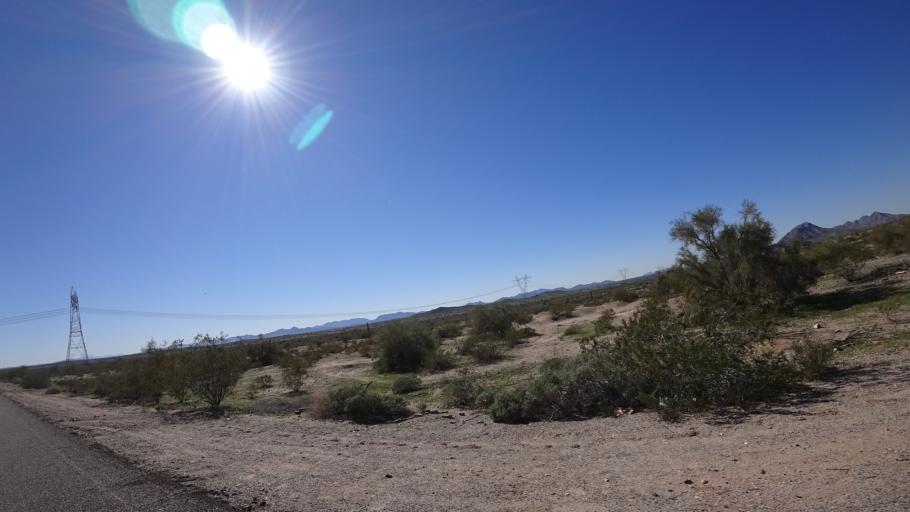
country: US
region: Arizona
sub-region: Maricopa County
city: Buckeye
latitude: 33.3098
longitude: -112.4656
